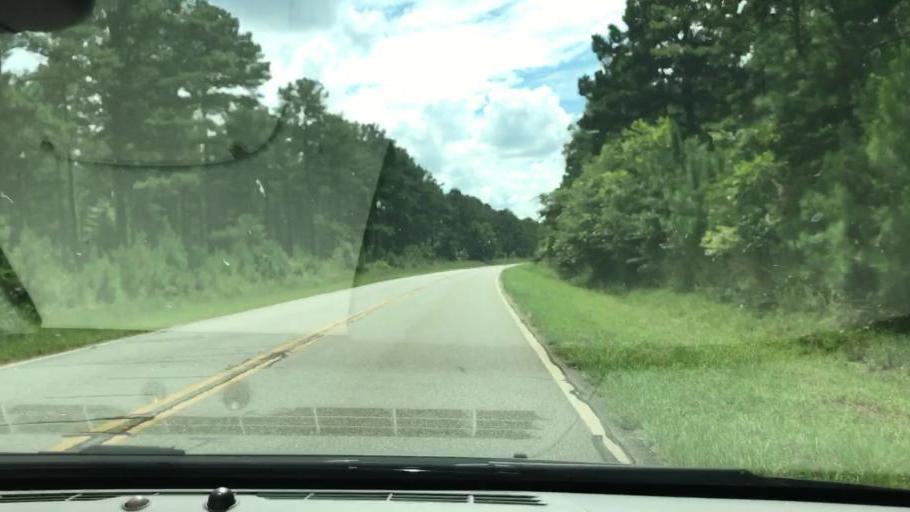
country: US
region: Georgia
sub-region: Quitman County
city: Georgetown
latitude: 32.0054
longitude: -85.0339
